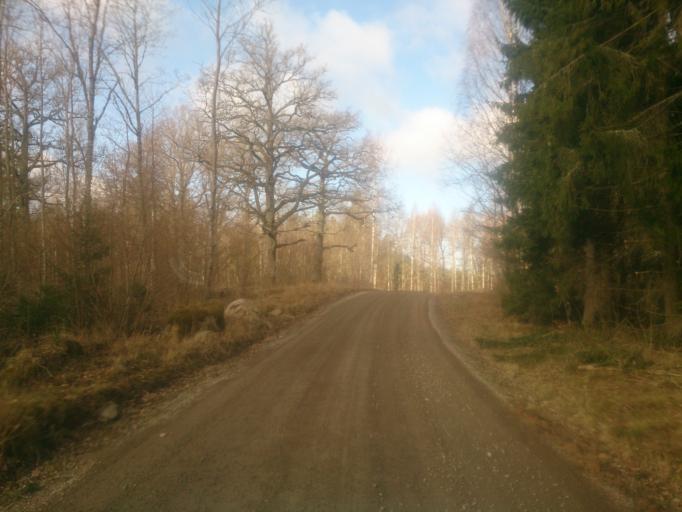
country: SE
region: OEstergoetland
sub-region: Atvidabergs Kommun
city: Atvidaberg
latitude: 58.1838
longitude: 16.1405
